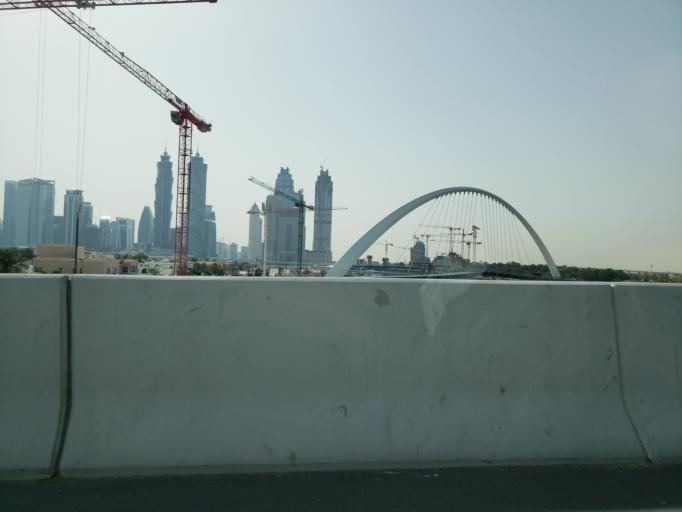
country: AE
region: Dubai
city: Dubai
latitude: 25.1910
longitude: 55.2429
